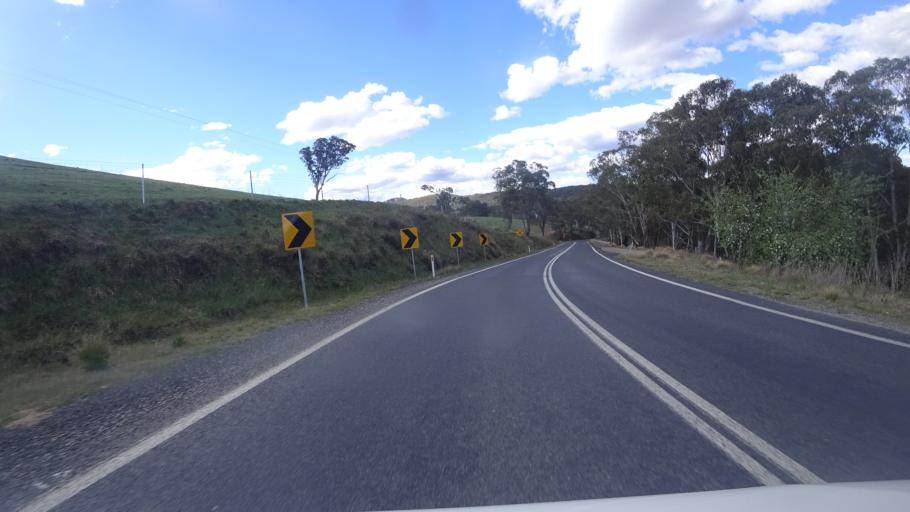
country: AU
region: New South Wales
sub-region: Lithgow
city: Bowenfels
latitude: -33.5518
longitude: 150.1455
